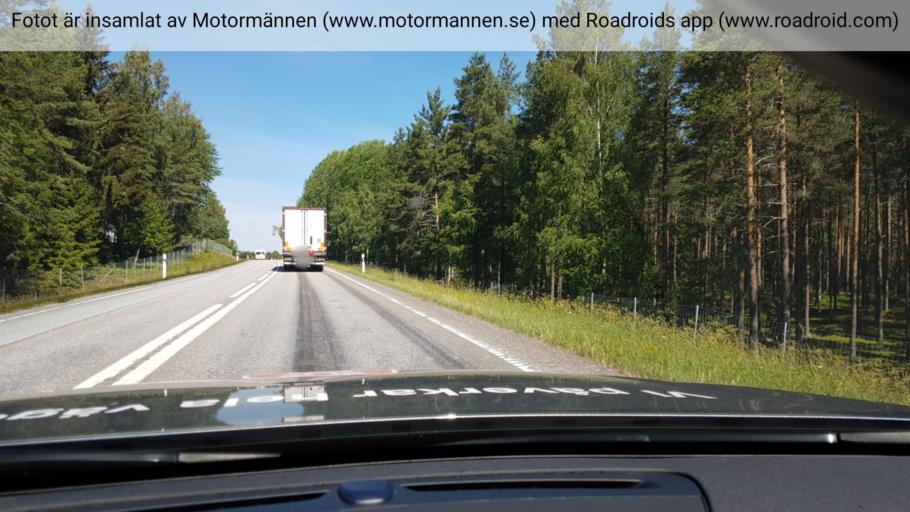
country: SE
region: OErebro
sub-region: Hallsbergs Kommun
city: Palsboda
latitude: 58.9414
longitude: 15.4253
